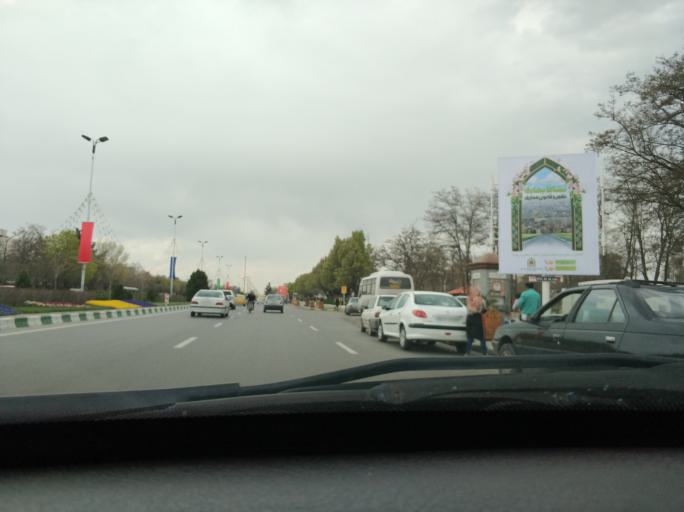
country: IR
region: Razavi Khorasan
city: Mashhad
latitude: 36.2558
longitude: 59.6111
